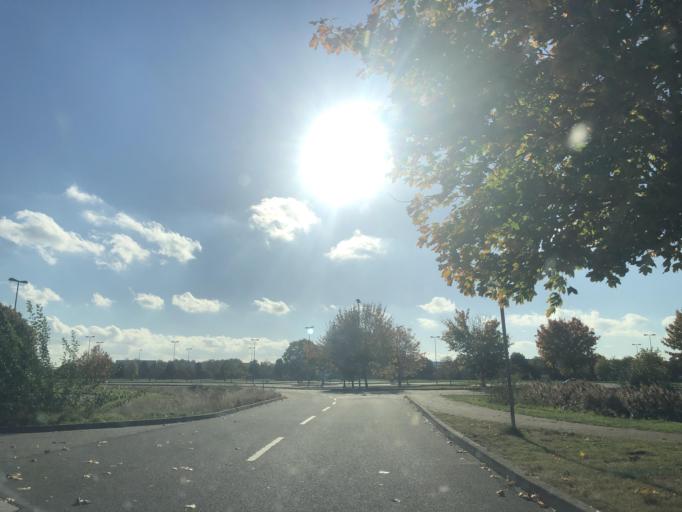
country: DE
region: Mecklenburg-Vorpommern
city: Wittenburg
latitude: 53.5067
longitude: 11.0975
